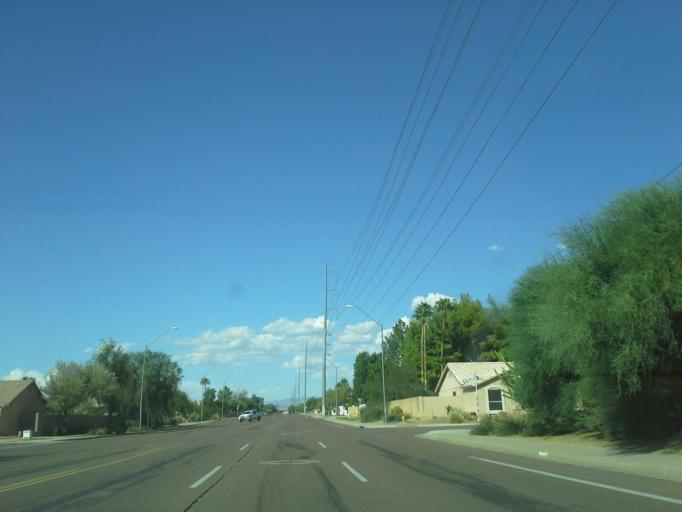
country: US
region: Arizona
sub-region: Maricopa County
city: Paradise Valley
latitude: 33.6570
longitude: -112.0136
